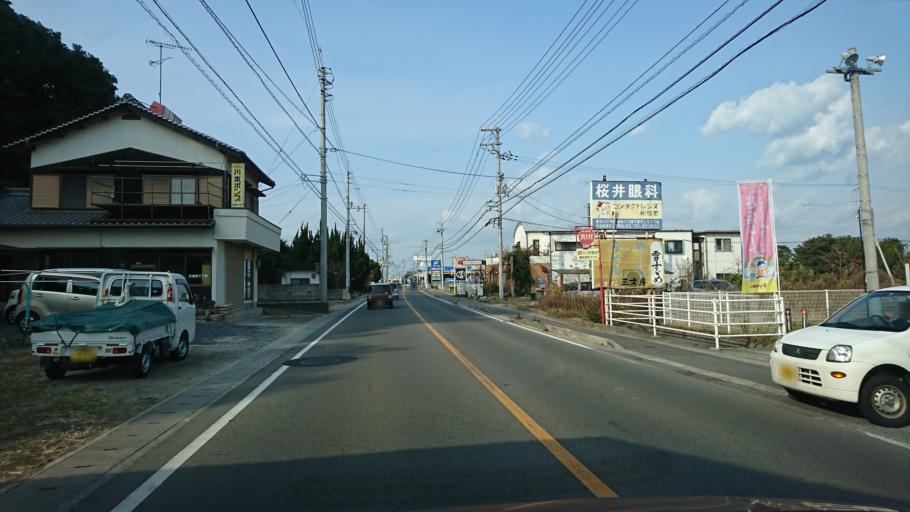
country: JP
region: Ehime
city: Saijo
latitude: 34.0302
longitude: 133.0364
